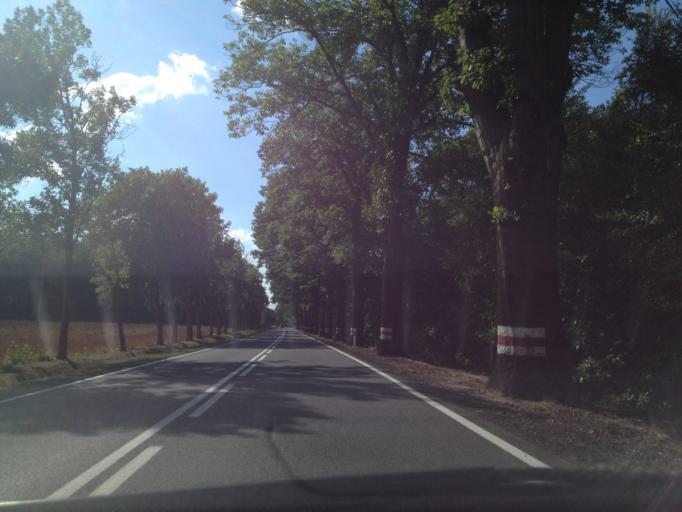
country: PL
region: Lubusz
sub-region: Powiat zarski
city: Lipinki Luzyckie
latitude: 51.6352
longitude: 14.9272
